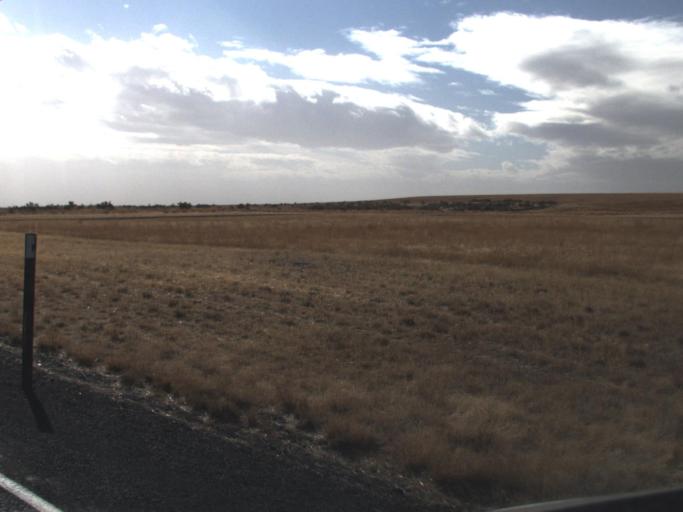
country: US
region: Washington
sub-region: Okanogan County
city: Coulee Dam
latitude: 47.5674
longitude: -118.7859
